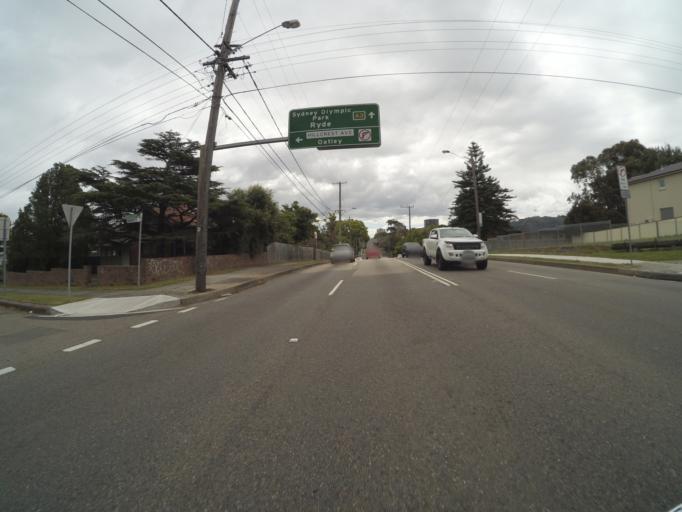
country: AU
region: New South Wales
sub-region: Kogarah
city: Hurstville Grove
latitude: -33.9718
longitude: 151.0998
